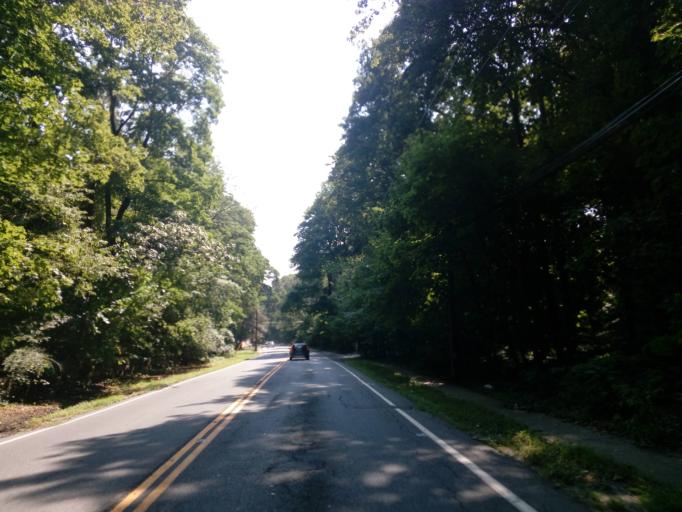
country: US
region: New York
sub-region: Nassau County
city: Locust Valley
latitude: 40.8722
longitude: -73.5946
